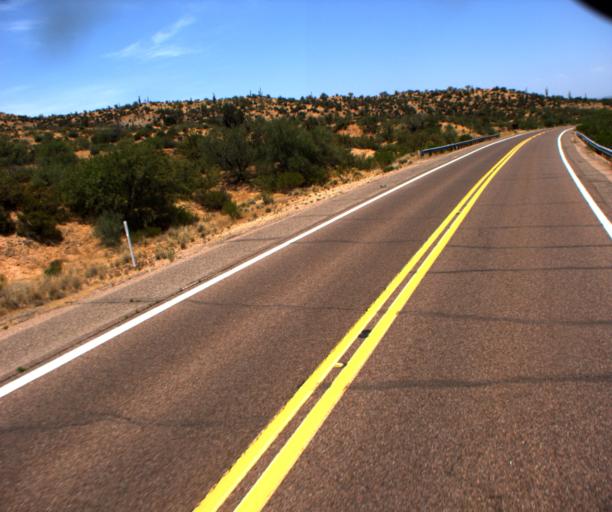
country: US
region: Arizona
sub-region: Gila County
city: Tonto Basin
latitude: 33.7801
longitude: -111.2636
